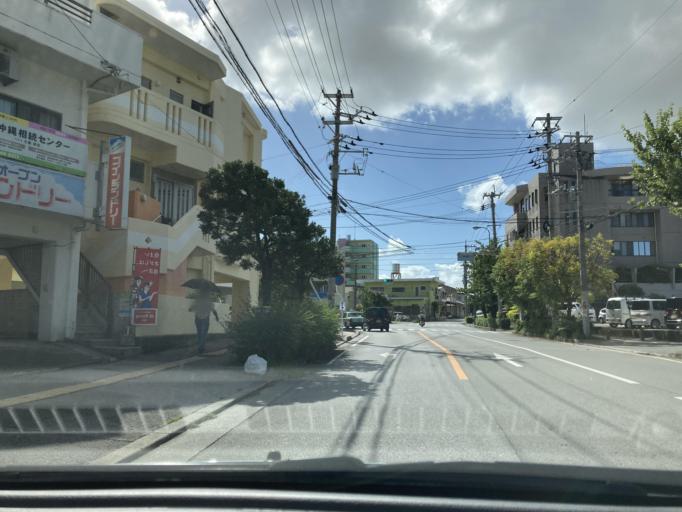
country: JP
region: Okinawa
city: Naha-shi
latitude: 26.2069
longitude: 127.6839
